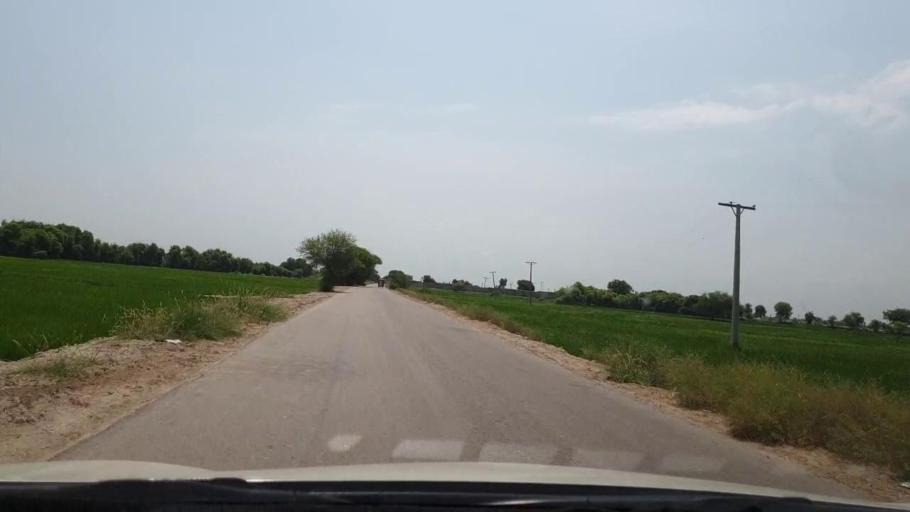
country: PK
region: Sindh
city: Ratodero
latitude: 27.8157
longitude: 68.2483
